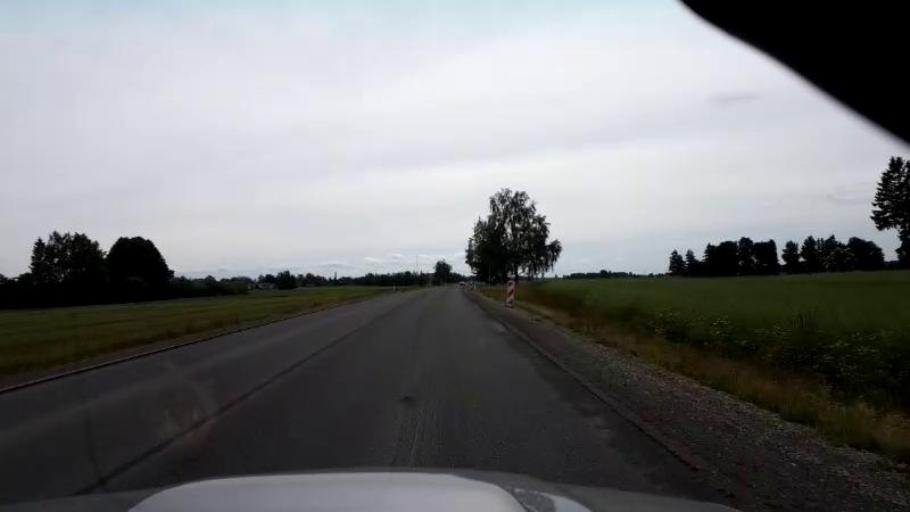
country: LV
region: Bauskas Rajons
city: Bauska
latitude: 56.3169
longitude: 24.3257
